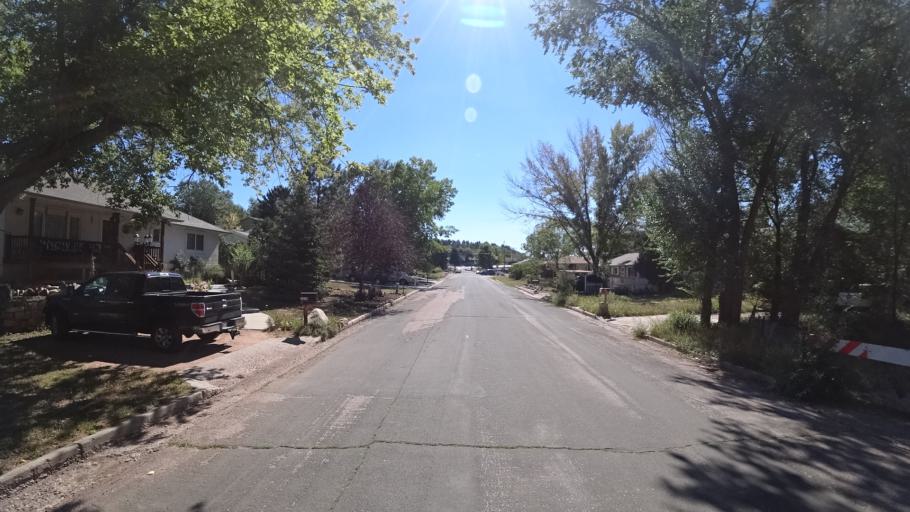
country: US
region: Colorado
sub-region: El Paso County
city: Manitou Springs
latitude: 38.8589
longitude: -104.8756
